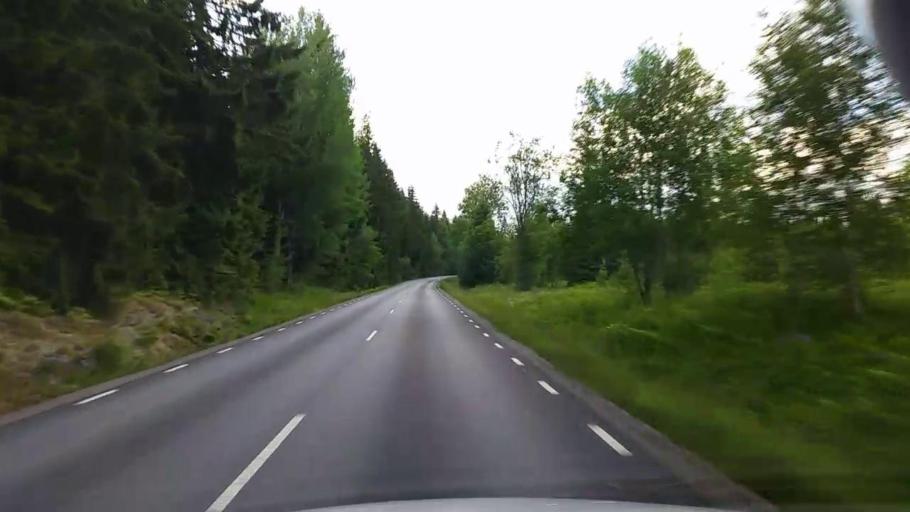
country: SE
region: Vaestmanland
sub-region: Kopings Kommun
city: Kolsva
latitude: 59.6339
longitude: 15.8201
